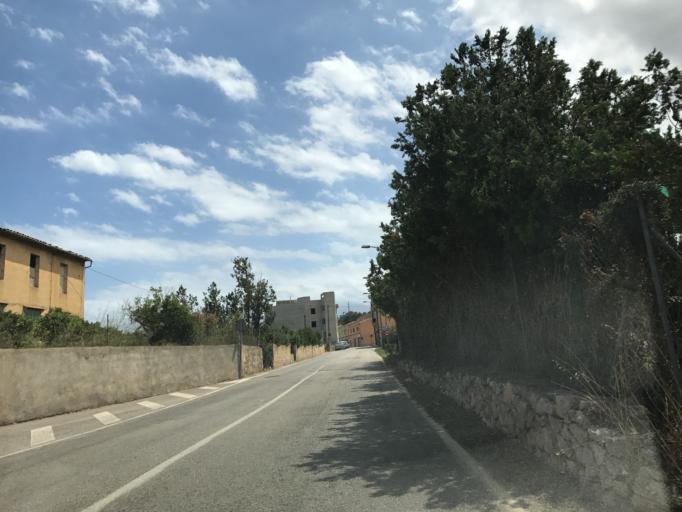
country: ES
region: Balearic Islands
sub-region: Illes Balears
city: Son Servera
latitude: 39.6274
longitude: 3.3565
